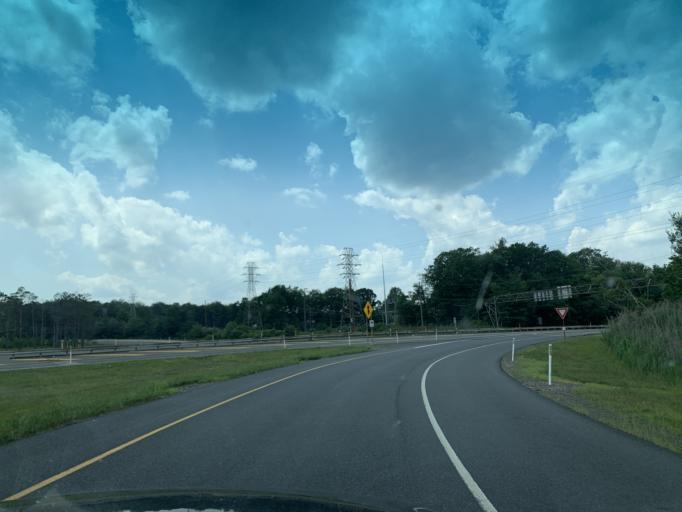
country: US
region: Pennsylvania
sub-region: Schuylkill County
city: Frackville
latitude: 40.7746
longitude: -76.2252
